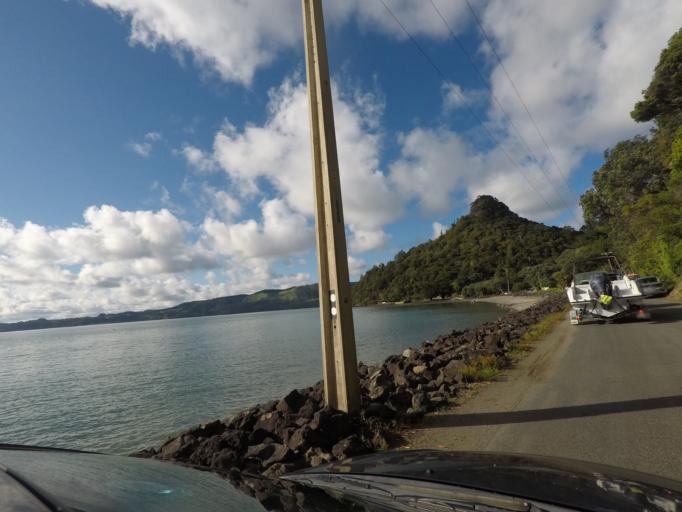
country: NZ
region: Auckland
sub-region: Auckland
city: Titirangi
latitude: -37.0141
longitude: 174.5593
